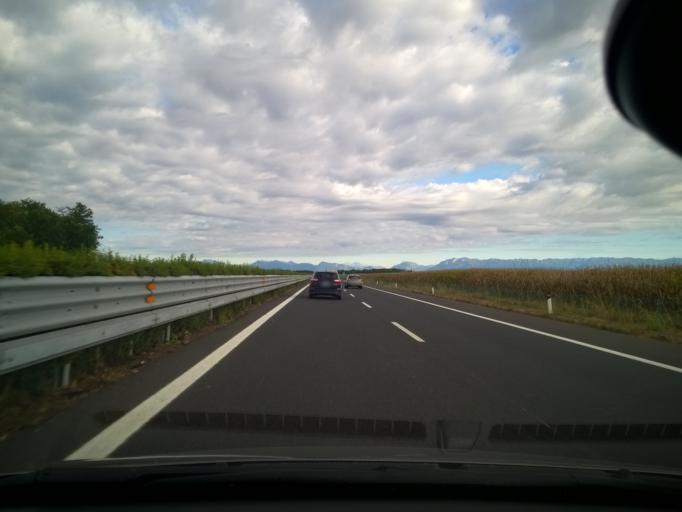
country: IT
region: Friuli Venezia Giulia
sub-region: Provincia di Udine
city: Bicinicco
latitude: 45.9324
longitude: 13.2693
